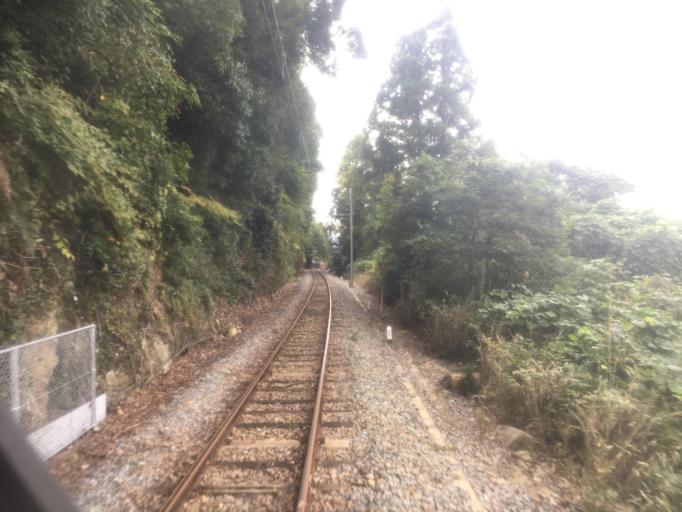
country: JP
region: Hyogo
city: Nishiwaki
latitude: 34.9799
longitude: 134.9862
